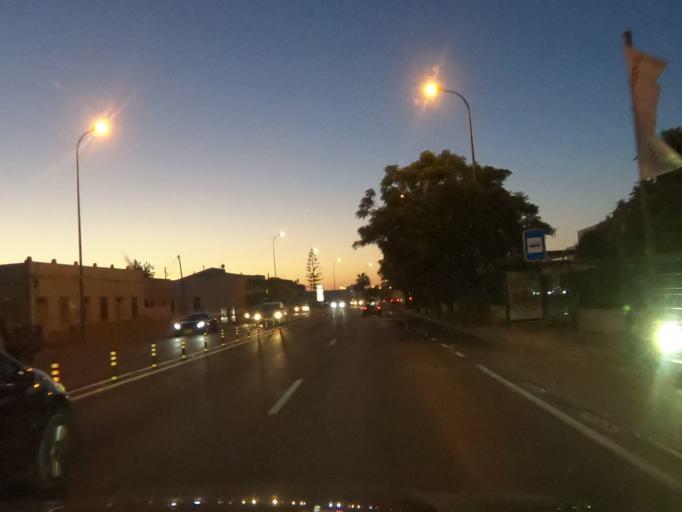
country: PT
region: Faro
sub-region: Faro
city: Faro
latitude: 37.0305
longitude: -7.9478
